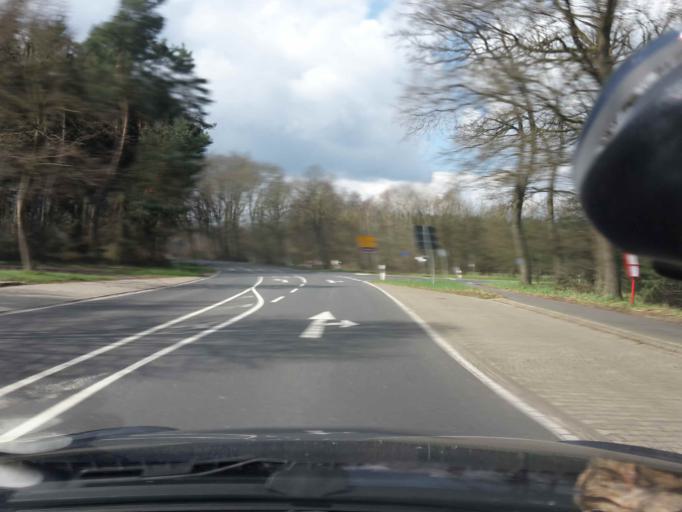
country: DE
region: Lower Saxony
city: Asendorf
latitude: 53.2869
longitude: 10.0011
